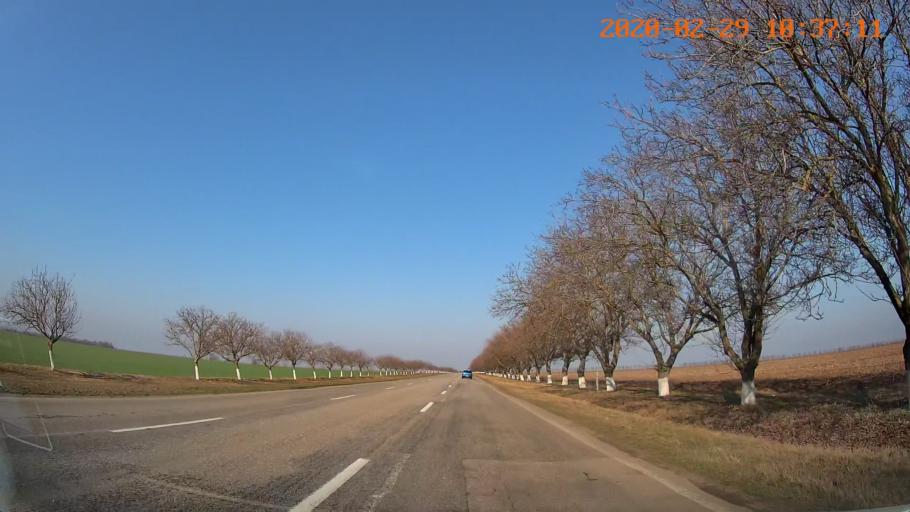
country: MD
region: Anenii Noi
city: Varnita
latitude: 47.0034
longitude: 29.4936
